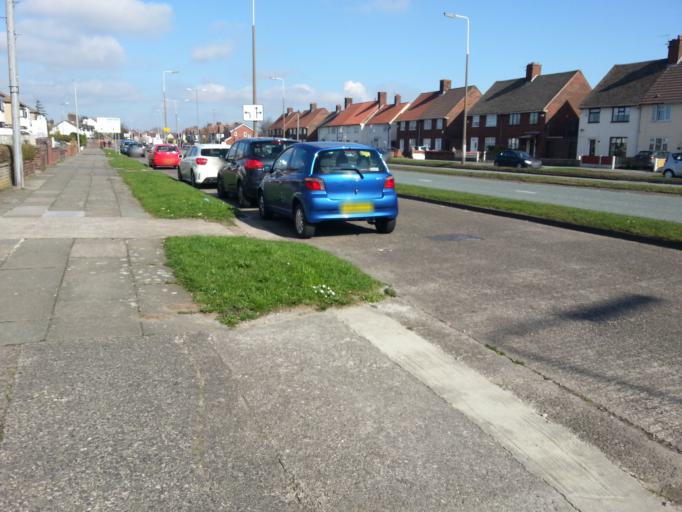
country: GB
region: England
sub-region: Knowsley
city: Huyton
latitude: 53.3599
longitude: -2.8535
